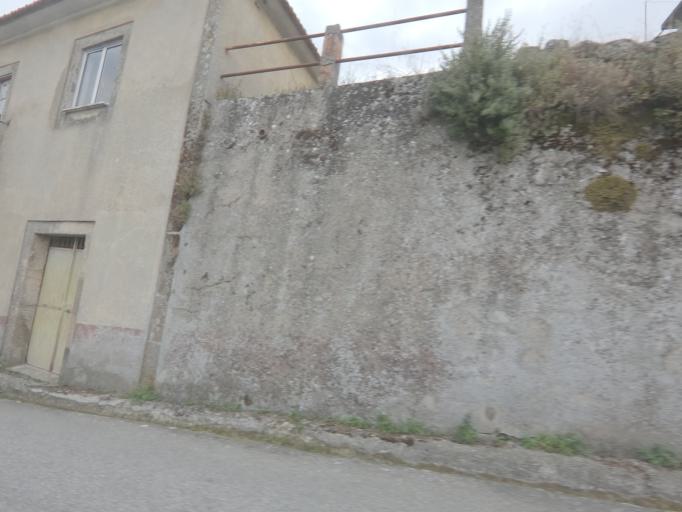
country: PT
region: Viseu
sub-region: Armamar
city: Armamar
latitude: 41.1237
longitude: -7.6625
